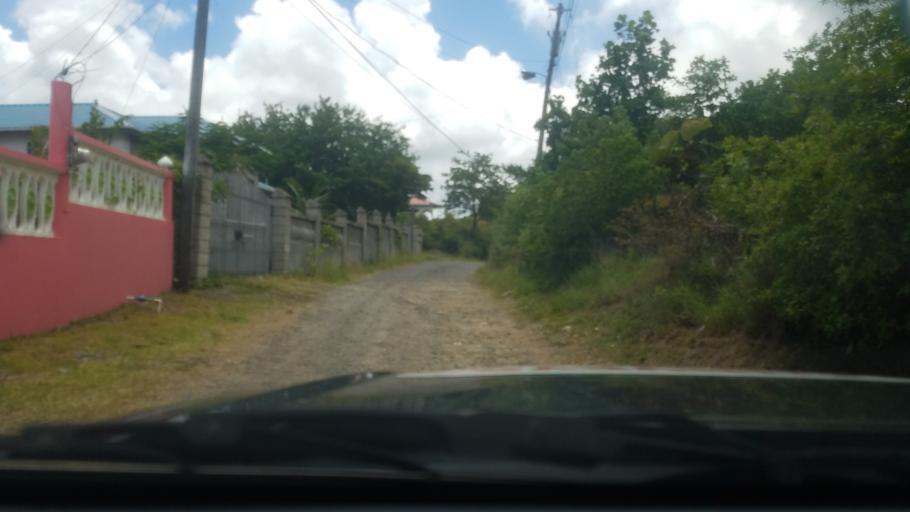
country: LC
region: Dennery Quarter
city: Dennery
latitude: 13.9193
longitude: -60.8984
